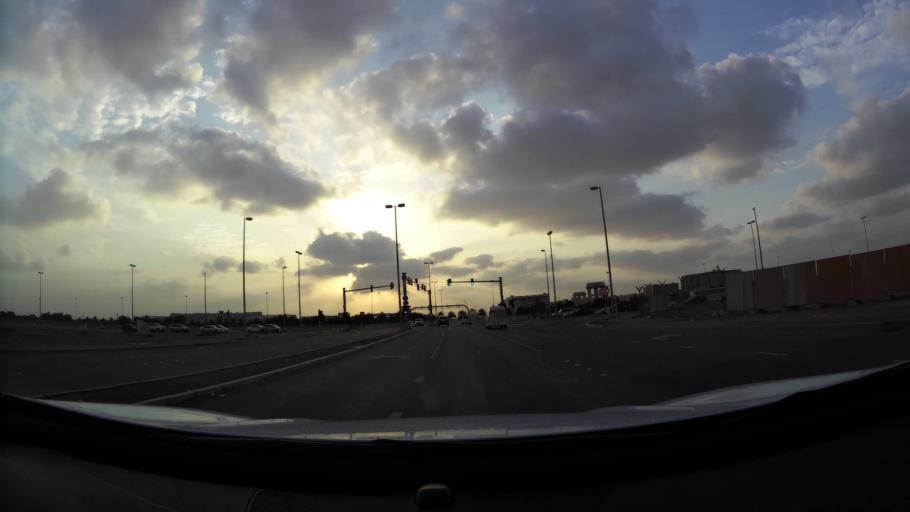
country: AE
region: Abu Dhabi
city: Abu Dhabi
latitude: 24.3605
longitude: 54.5289
